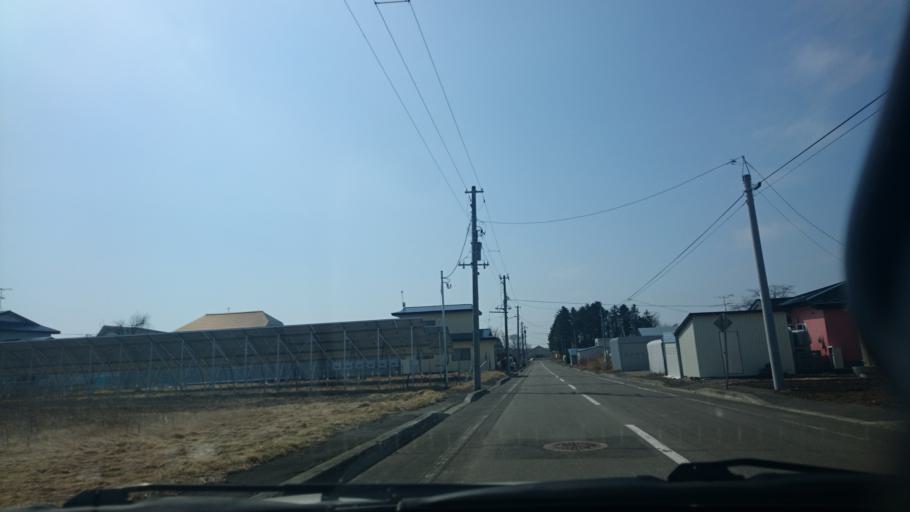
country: JP
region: Hokkaido
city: Otofuke
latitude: 43.0946
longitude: 143.2282
